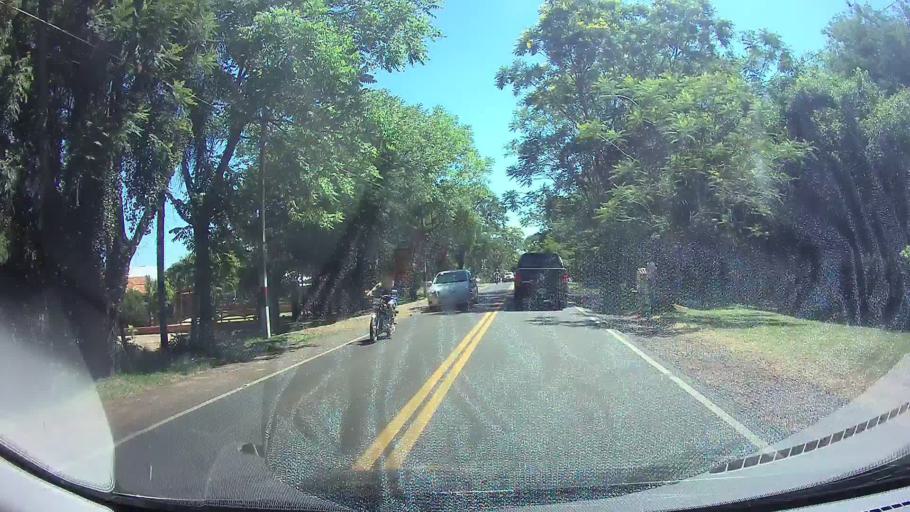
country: PY
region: Central
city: Aregua
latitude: -25.3274
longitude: -57.3975
